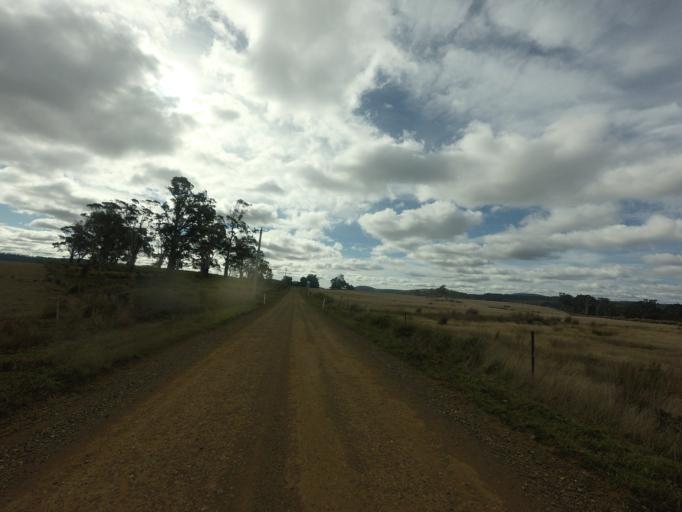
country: AU
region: Tasmania
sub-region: Brighton
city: Bridgewater
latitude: -42.4389
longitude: 147.3857
